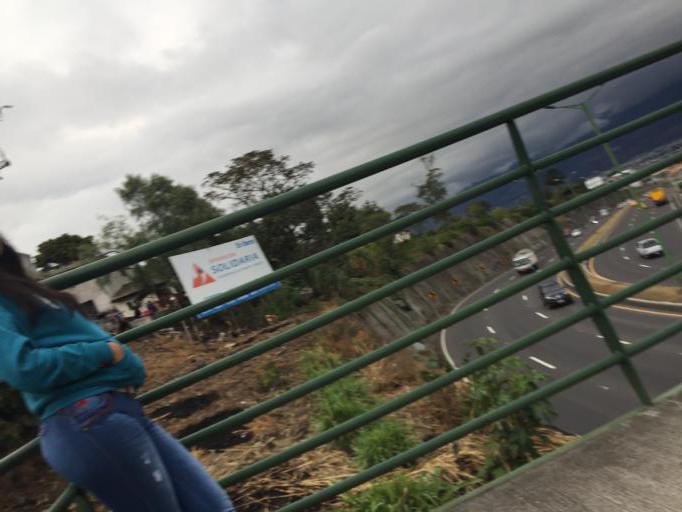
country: EC
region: Imbabura
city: Atuntaqui
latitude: 0.3423
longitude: -78.1740
